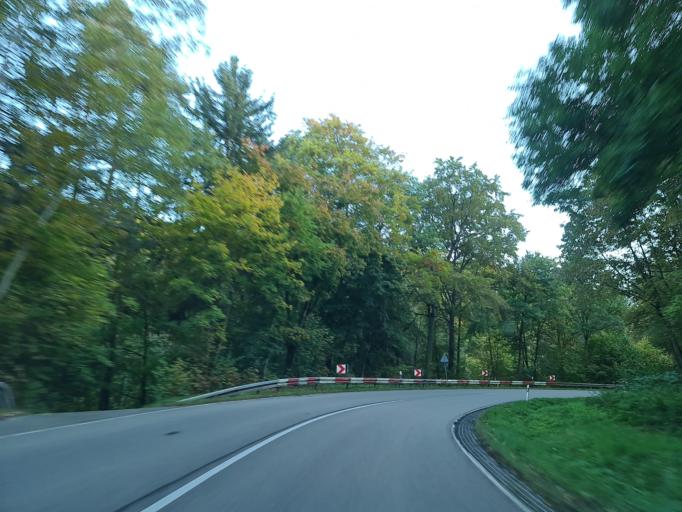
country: DE
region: Saxony
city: Elsterberg
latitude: 50.5774
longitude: 12.1297
